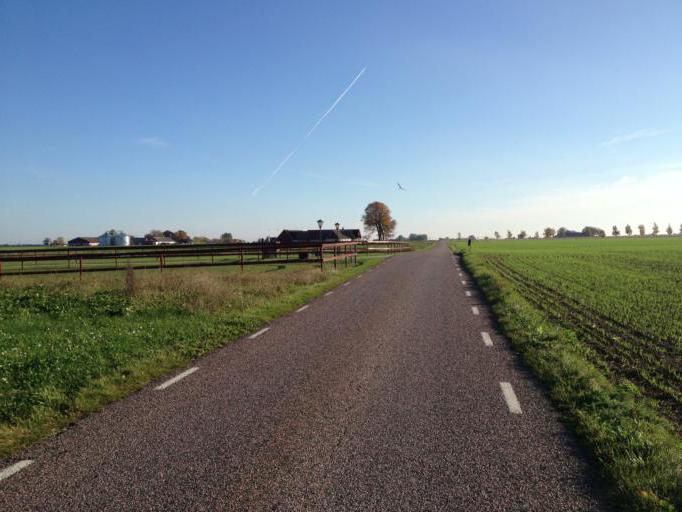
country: SE
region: Skane
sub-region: Kavlinge Kommun
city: Loddekopinge
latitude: 55.7825
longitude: 13.0393
